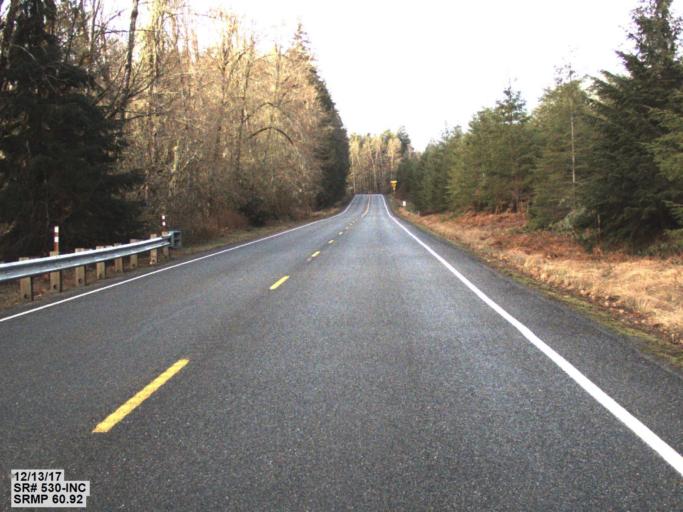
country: US
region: Washington
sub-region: Snohomish County
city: Darrington
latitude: 48.4011
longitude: -121.5534
